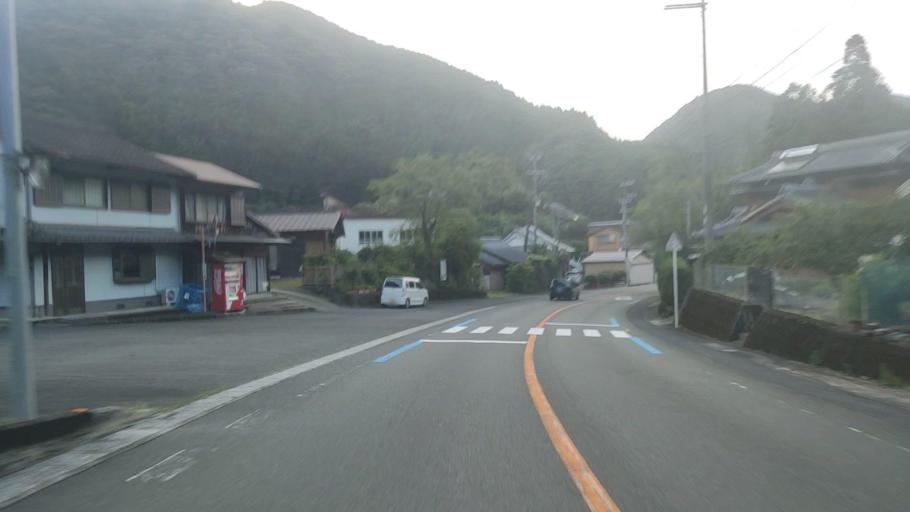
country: JP
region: Wakayama
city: Tanabe
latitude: 33.8126
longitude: 135.5499
